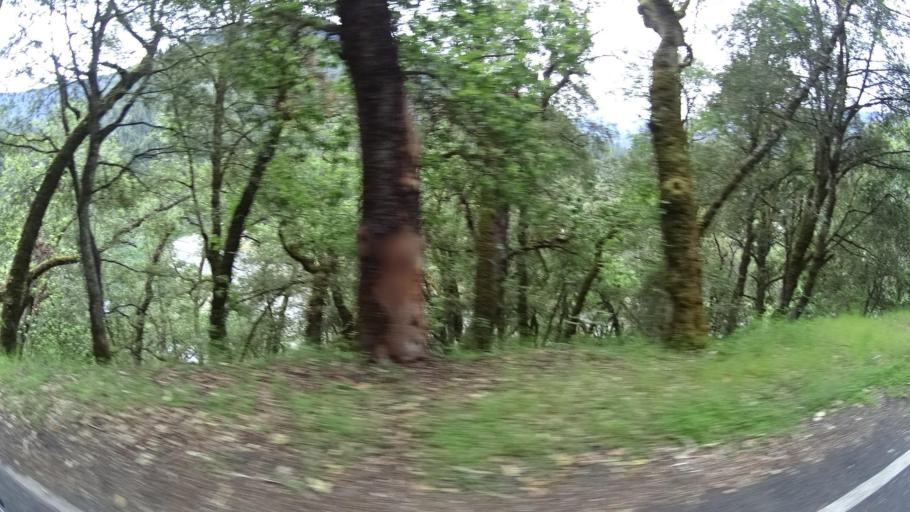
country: US
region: California
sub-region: Humboldt County
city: Willow Creek
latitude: 40.9496
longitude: -123.6161
